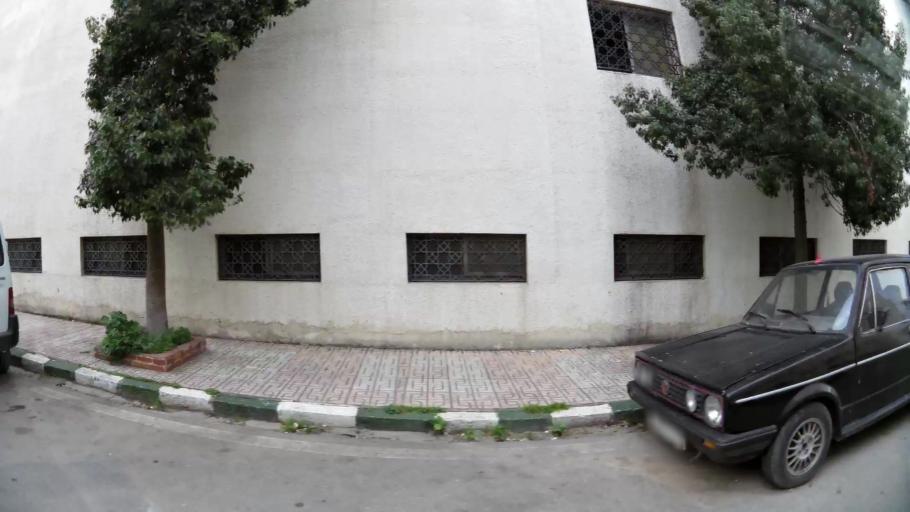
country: MA
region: Tanger-Tetouan
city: Tetouan
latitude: 35.5720
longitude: -5.3514
